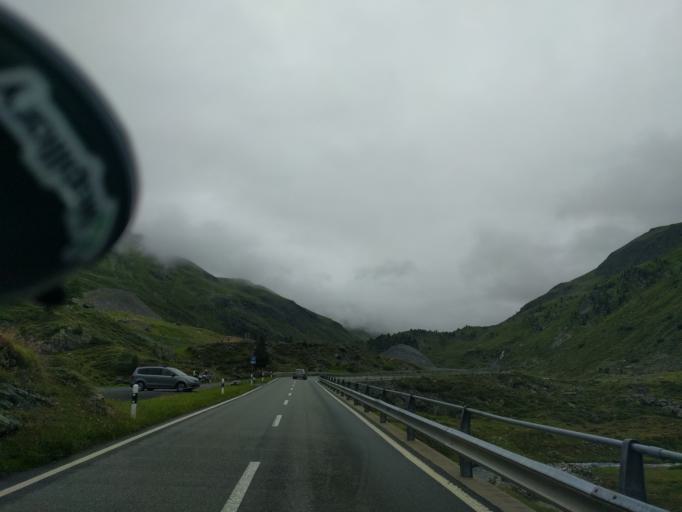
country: CH
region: Grisons
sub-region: Praettigau/Davos District
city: Davos
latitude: 46.7865
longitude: 9.9193
